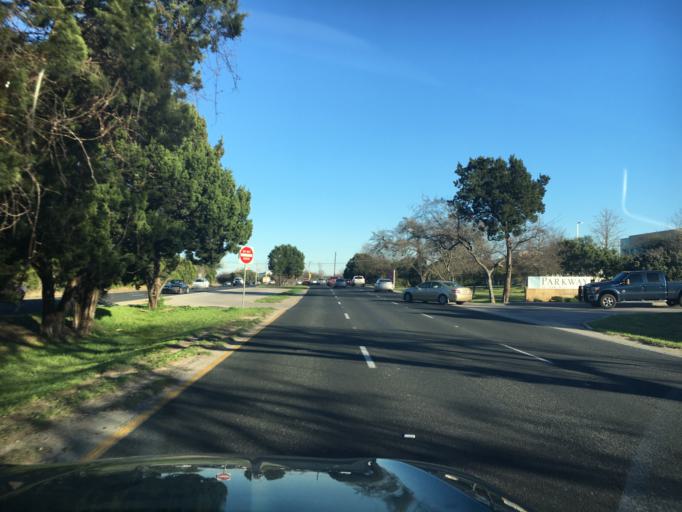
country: US
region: Texas
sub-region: Travis County
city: Lost Creek
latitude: 30.2410
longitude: -97.8357
